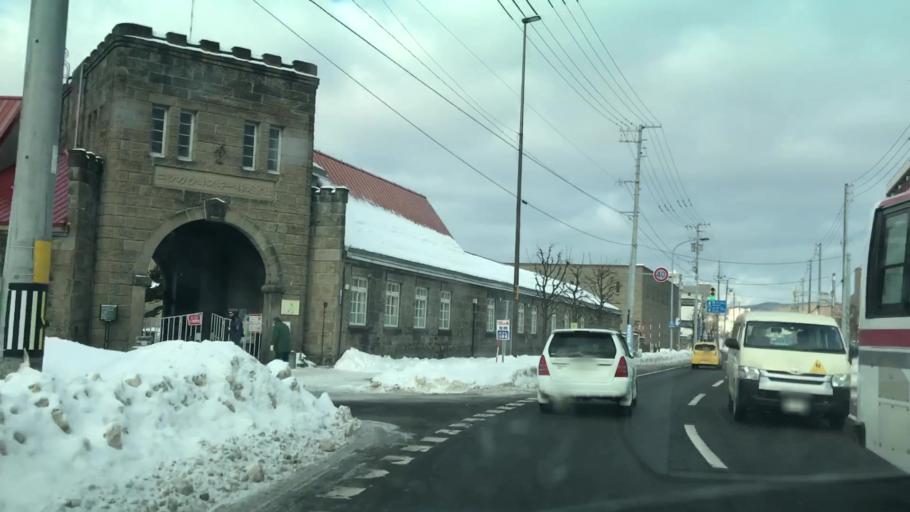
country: JP
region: Hokkaido
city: Yoichi
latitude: 43.1873
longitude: 140.7922
